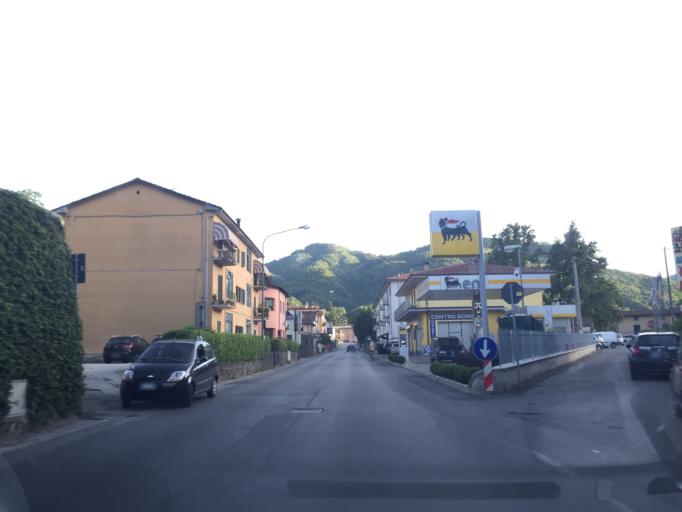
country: IT
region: Tuscany
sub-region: Provincia di Lucca
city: Castelnuovo di Garfagnana
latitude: 44.1065
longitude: 10.4098
